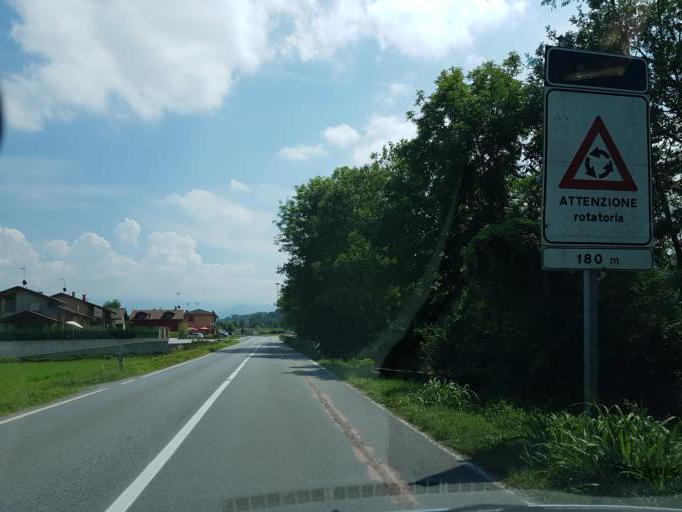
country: IT
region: Piedmont
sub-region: Provincia di Cuneo
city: San Rocco
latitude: 44.3927
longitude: 7.4571
